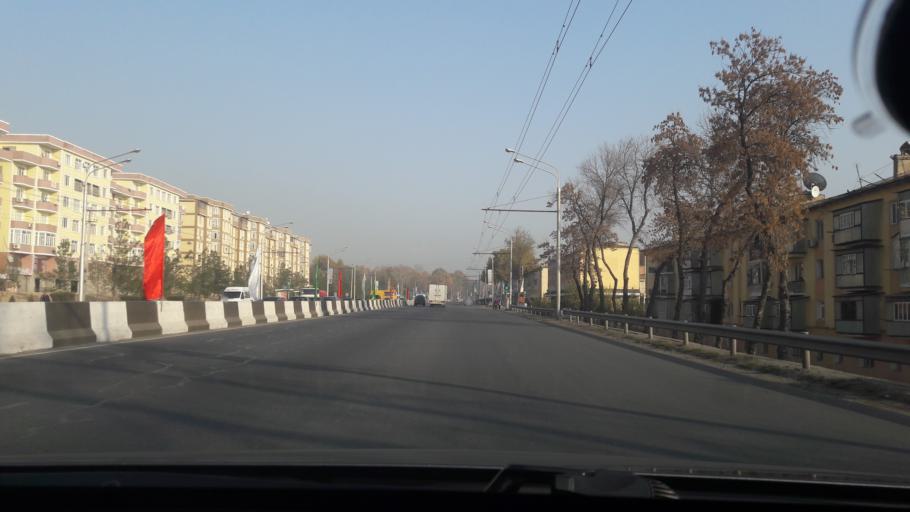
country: TJ
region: Dushanbe
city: Dushanbe
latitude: 38.5533
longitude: 68.8495
